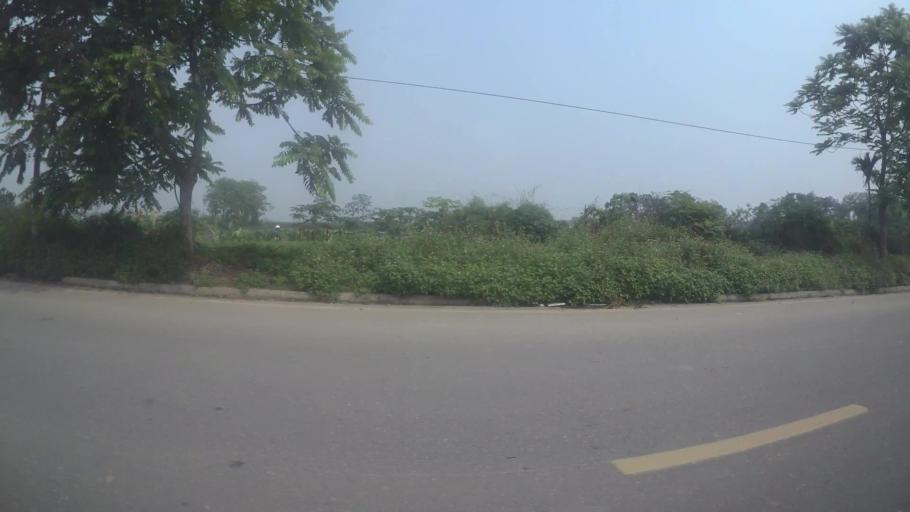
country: VN
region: Ha Noi
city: Quoc Oai
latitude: 20.9928
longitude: 105.5838
